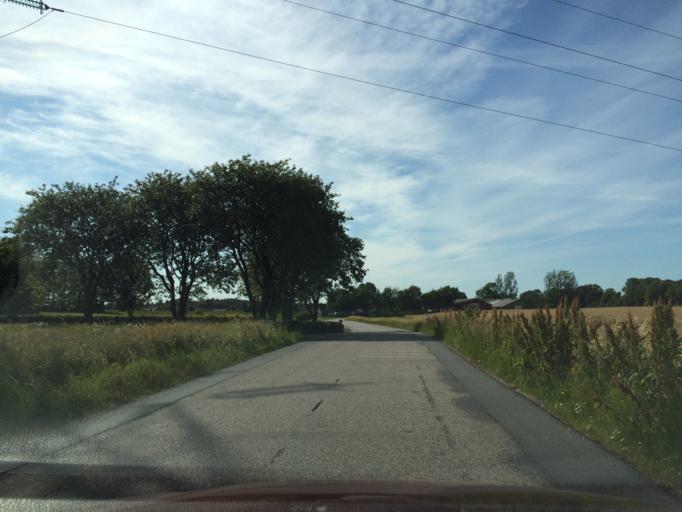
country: DK
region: Central Jutland
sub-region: Silkeborg Kommune
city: Silkeborg
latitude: 56.2234
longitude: 9.5694
